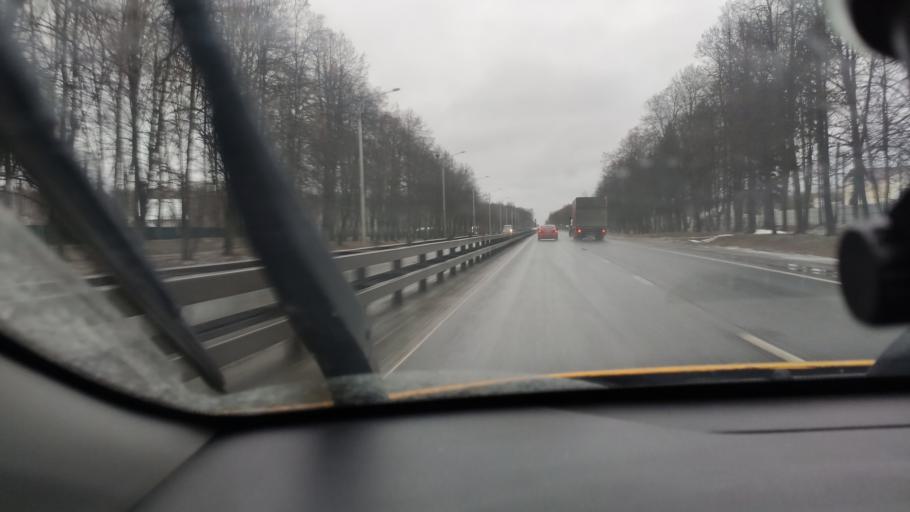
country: RU
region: Moskovskaya
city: Troitsk
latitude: 55.3546
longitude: 37.3454
